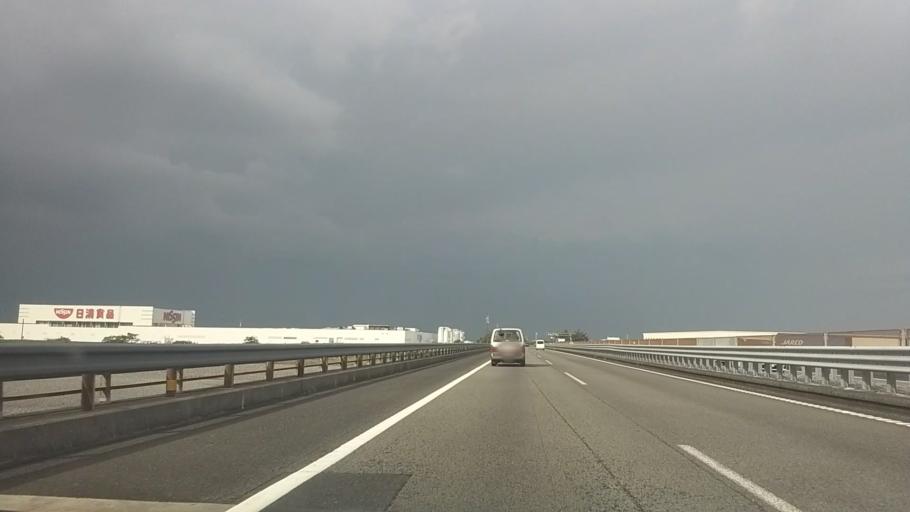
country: JP
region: Shizuoka
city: Fujieda
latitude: 34.8047
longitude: 138.2502
